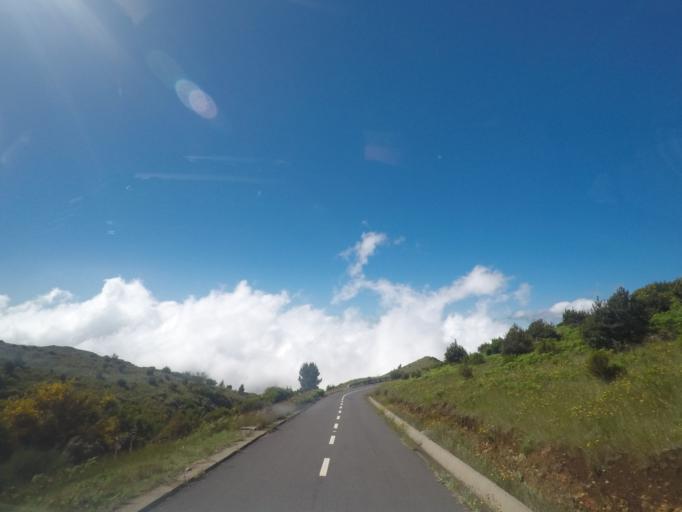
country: PT
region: Madeira
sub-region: Camara de Lobos
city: Curral das Freiras
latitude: 32.7068
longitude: -16.9393
